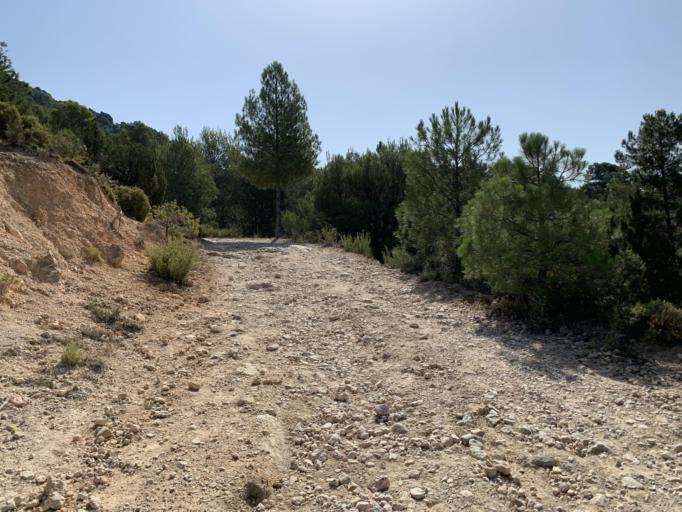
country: ES
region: Castille-La Mancha
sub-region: Provincia de Guadalajara
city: Ocentejo
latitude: 40.7630
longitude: -2.3903
